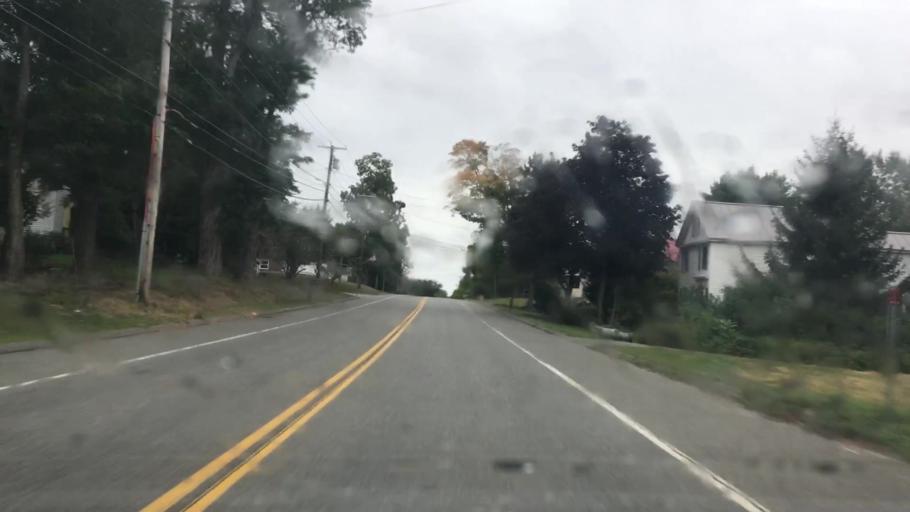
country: US
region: Maine
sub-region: Penobscot County
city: Orrington
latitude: 44.7287
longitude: -68.8274
